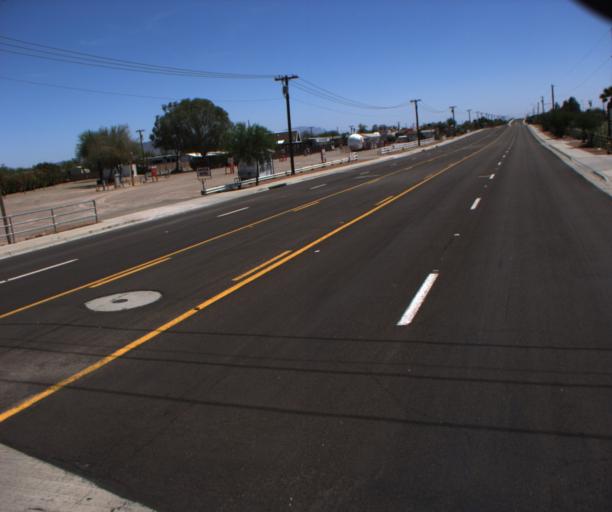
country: US
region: Arizona
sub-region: La Paz County
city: Quartzsite
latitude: 33.6750
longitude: -114.2172
